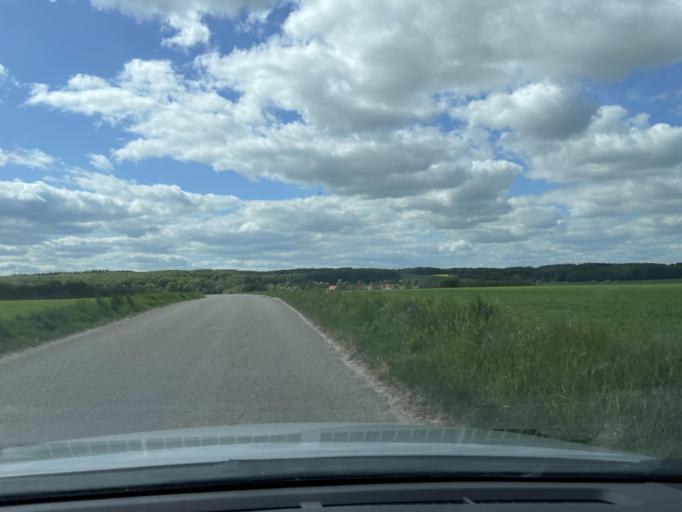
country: DK
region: Central Jutland
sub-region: Odder Kommune
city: Odder
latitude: 55.9099
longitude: 10.1178
